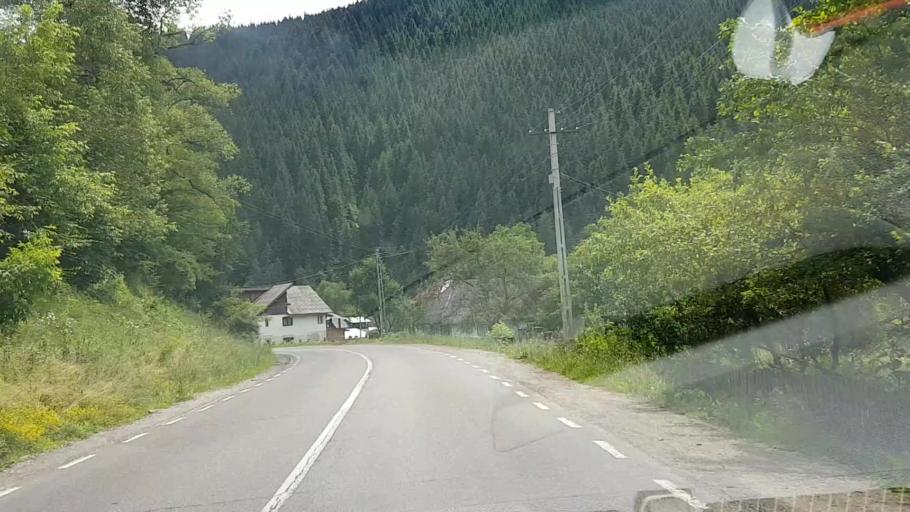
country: RO
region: Suceava
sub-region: Comuna Brosteni
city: Brosteni
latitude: 47.2177
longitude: 25.7379
